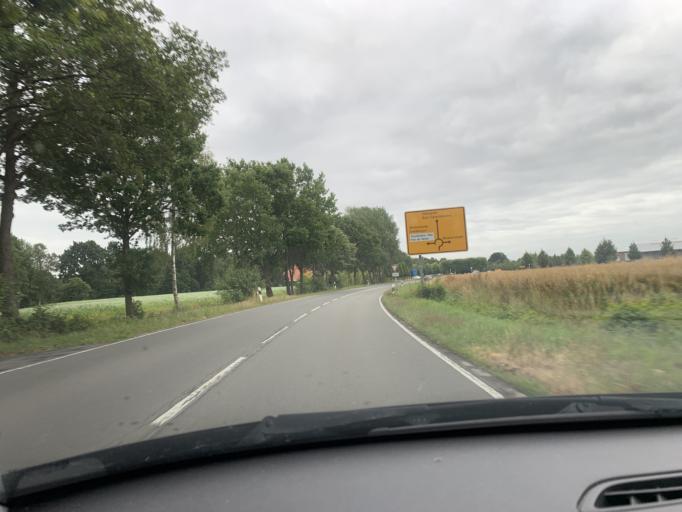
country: DE
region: Lower Saxony
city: Bad Zwischenahn
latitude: 53.2347
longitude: 7.9915
